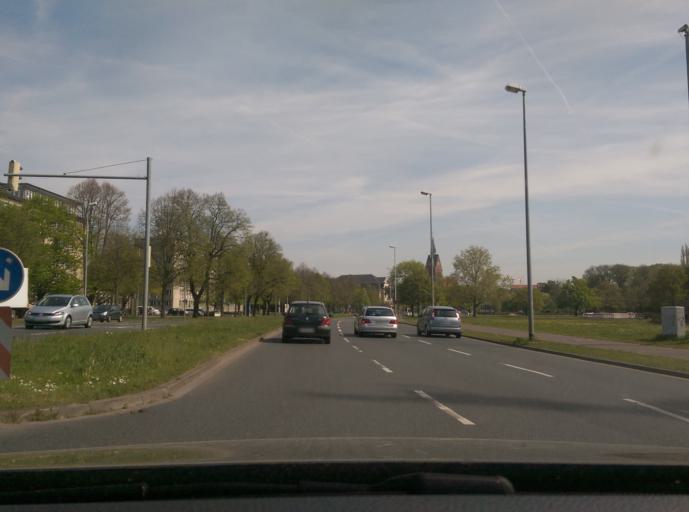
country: DE
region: Lower Saxony
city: Hannover
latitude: 52.3667
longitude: 9.7270
